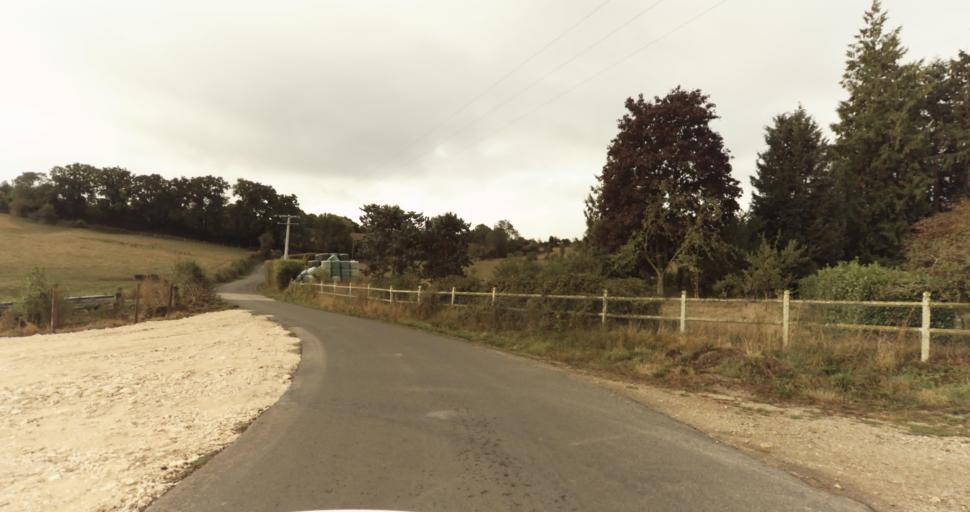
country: FR
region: Lower Normandy
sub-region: Departement de l'Orne
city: Trun
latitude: 48.9114
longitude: 0.0999
